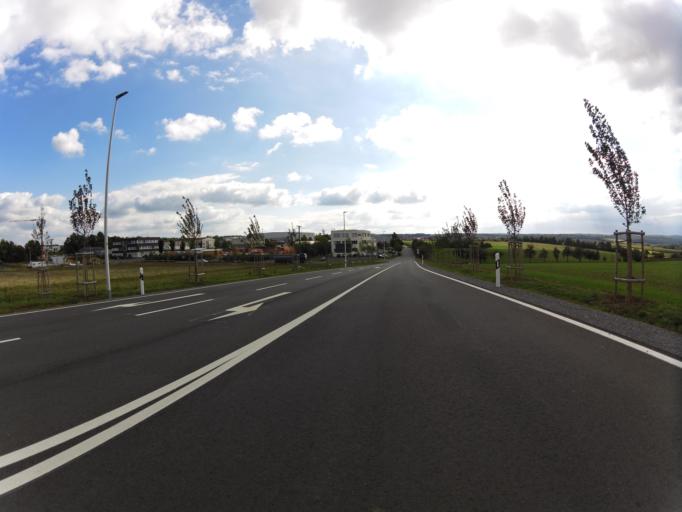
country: DE
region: Bavaria
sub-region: Regierungsbezirk Unterfranken
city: Waldbuttelbrunn
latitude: 49.7979
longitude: 9.8401
